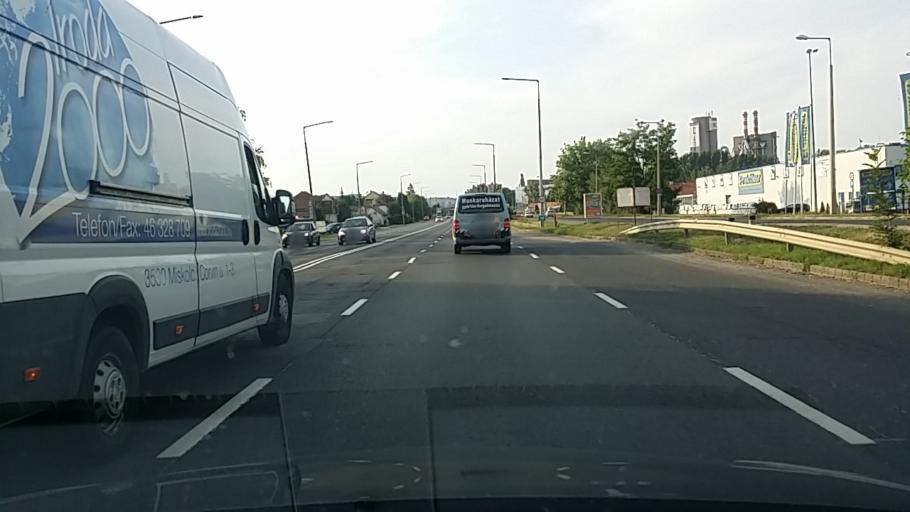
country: HU
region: Borsod-Abauj-Zemplen
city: Miskolc
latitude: 48.0570
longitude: 20.7971
